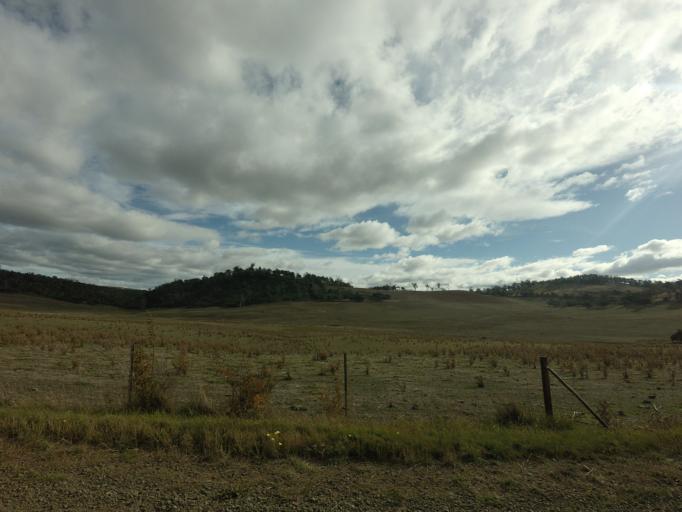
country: AU
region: Tasmania
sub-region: Brighton
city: Bridgewater
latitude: -42.4640
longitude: 147.2776
